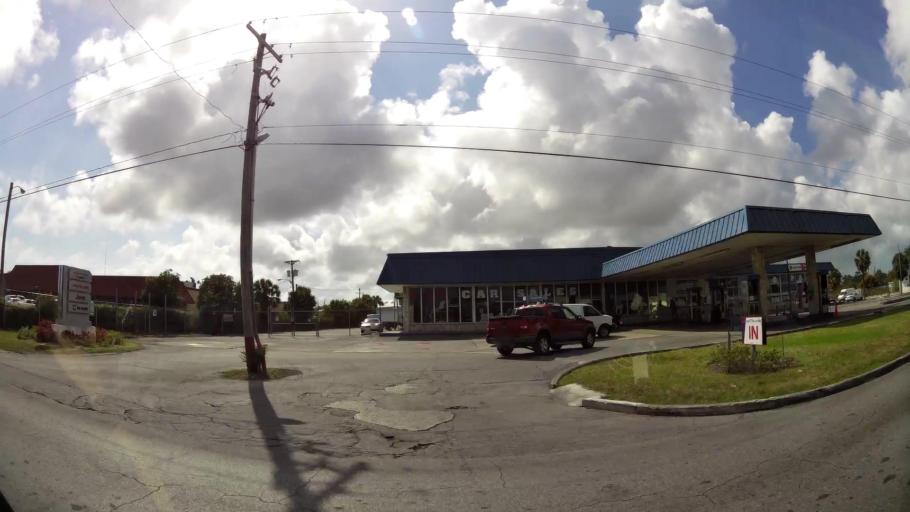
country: BS
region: Freeport
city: Freeport
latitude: 26.5327
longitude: -78.6972
